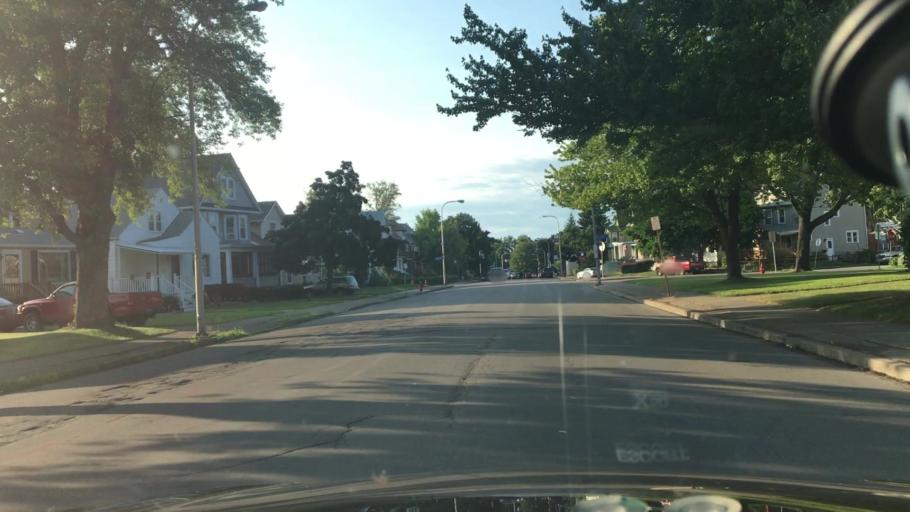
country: US
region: New York
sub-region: Erie County
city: West Seneca
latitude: 42.8436
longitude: -78.8092
